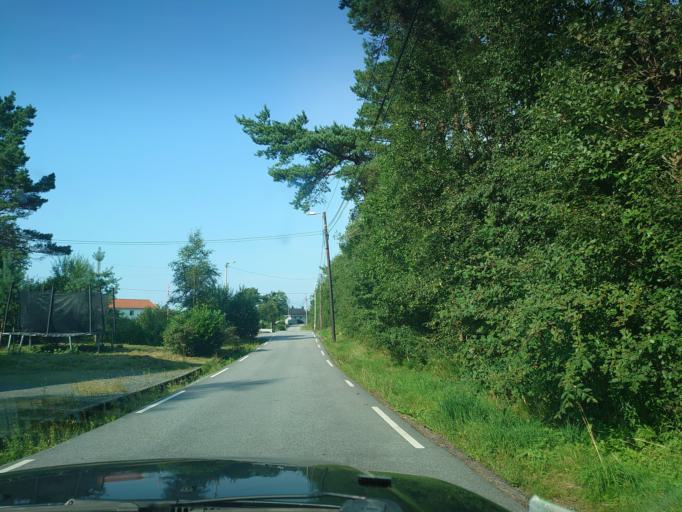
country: NO
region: Hordaland
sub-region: Bergen
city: Ytrebygda
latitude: 60.2664
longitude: 5.2589
